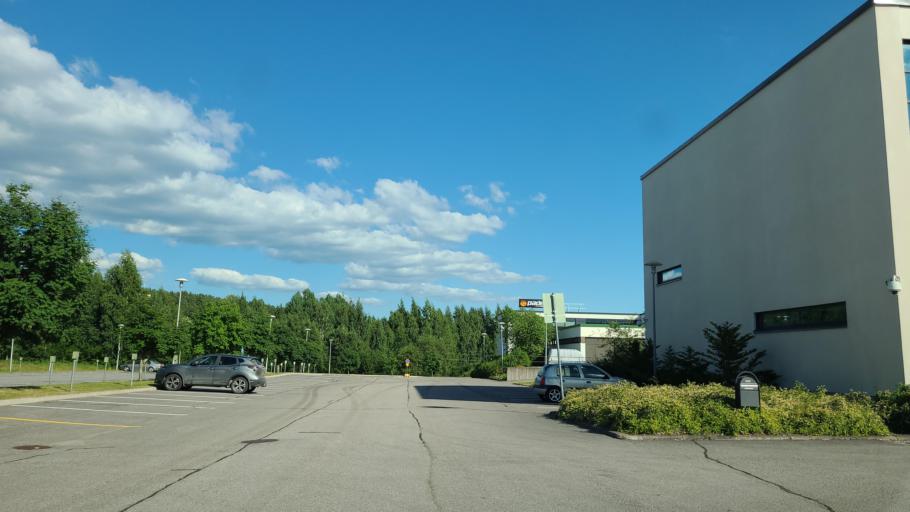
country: FI
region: Central Finland
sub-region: Jyvaeskylae
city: Jyvaeskylae
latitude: 62.2489
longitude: 25.7749
